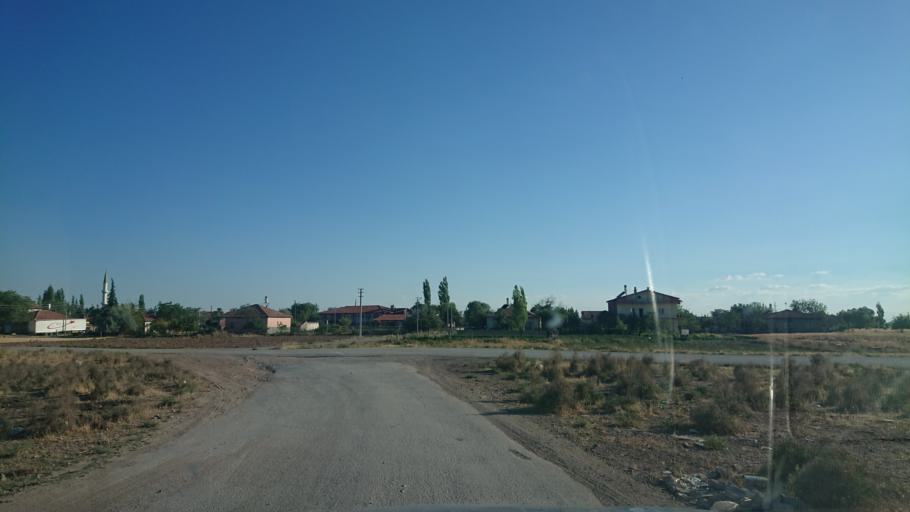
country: TR
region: Aksaray
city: Aksaray
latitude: 38.3868
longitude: 33.9913
